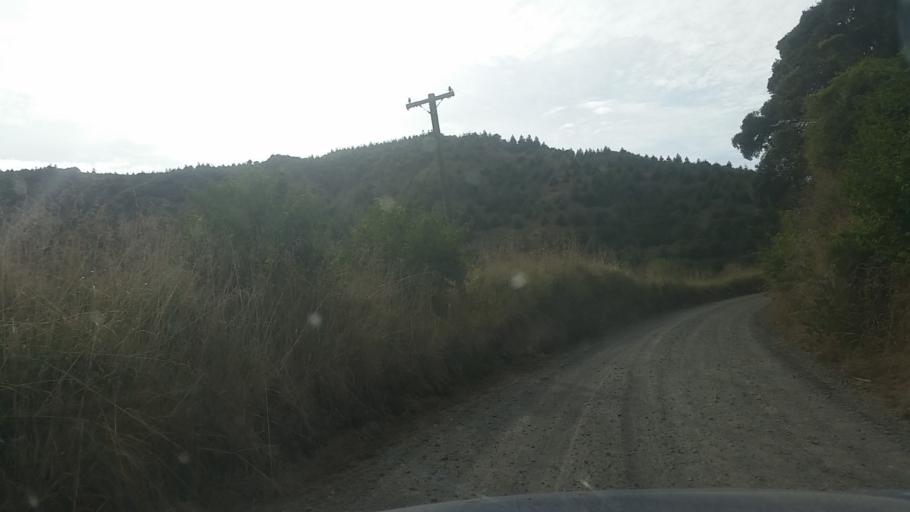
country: NZ
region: Taranaki
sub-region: New Plymouth District
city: Waitara
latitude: -39.1382
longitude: 174.7154
